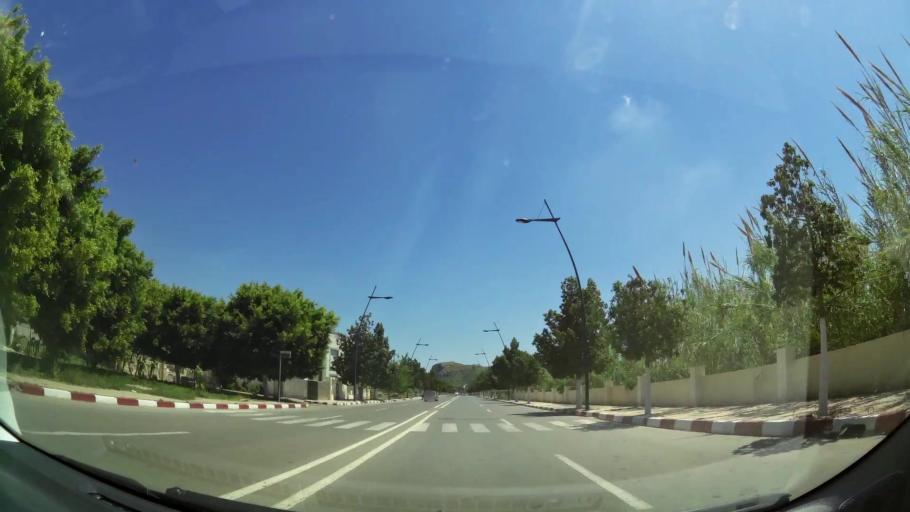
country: MA
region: Oriental
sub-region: Berkane-Taourirt
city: Madagh
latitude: 35.0721
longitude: -2.2181
